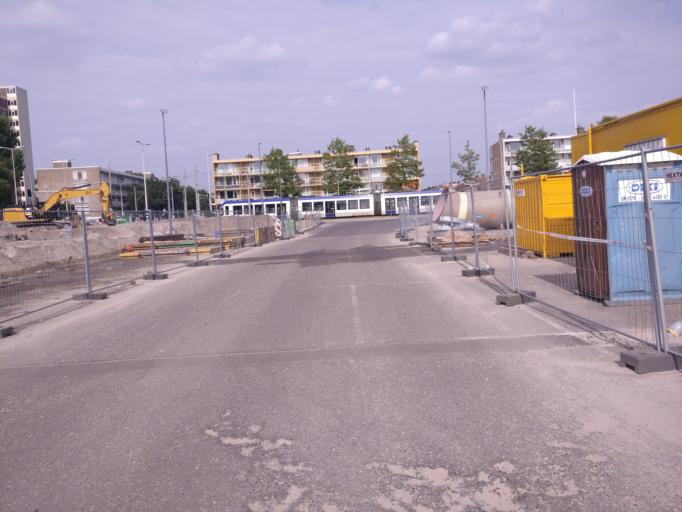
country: NL
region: South Holland
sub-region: Gemeente Den Haag
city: The Hague
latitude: 52.0577
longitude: 4.2636
